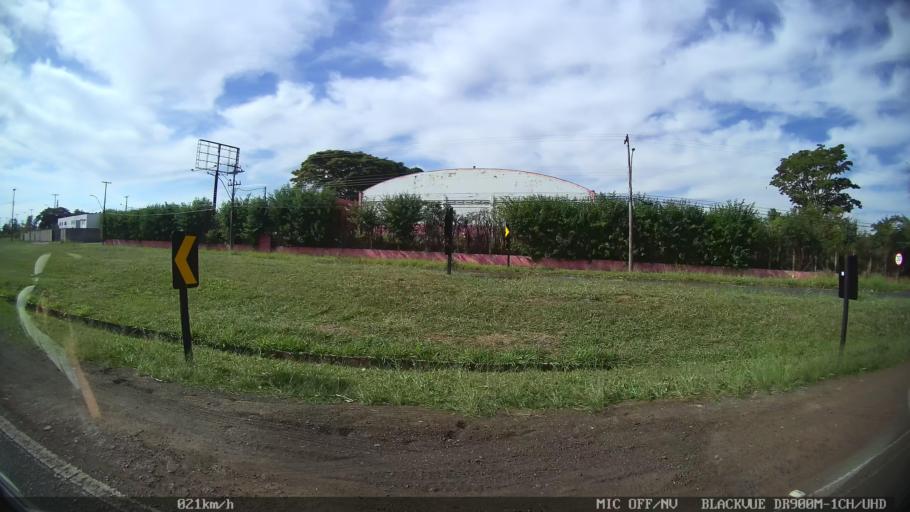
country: BR
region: Sao Paulo
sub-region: Araraquara
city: Araraquara
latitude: -21.8328
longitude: -48.1528
